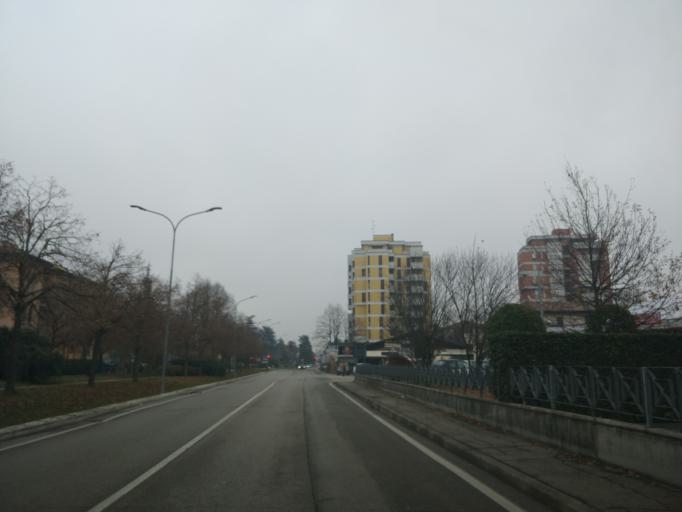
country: IT
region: Emilia-Romagna
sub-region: Provincia di Ferrara
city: Cento
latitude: 44.7224
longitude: 11.2919
